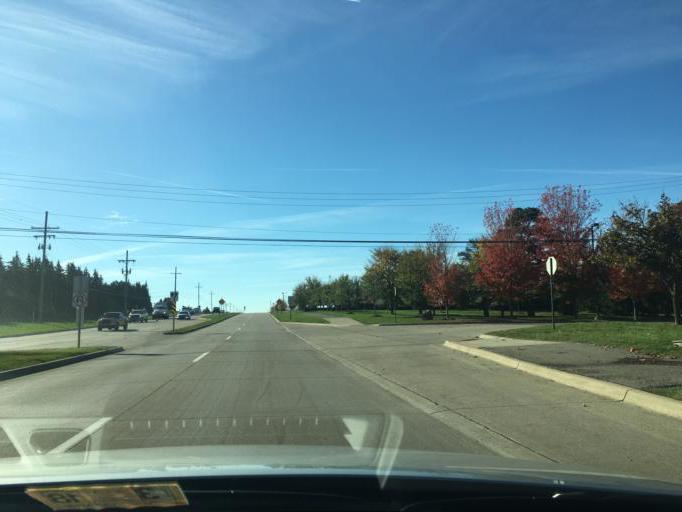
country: US
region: Michigan
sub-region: Wayne County
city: Northville
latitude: 42.4037
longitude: -83.5108
